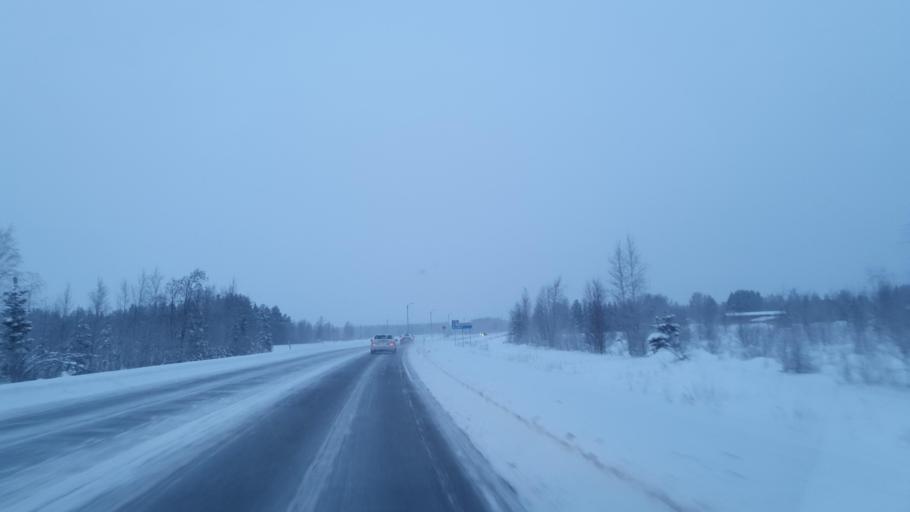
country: FI
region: Northern Ostrobothnia
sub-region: Oulunkaari
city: Utajaervi
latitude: 64.7486
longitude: 26.4301
